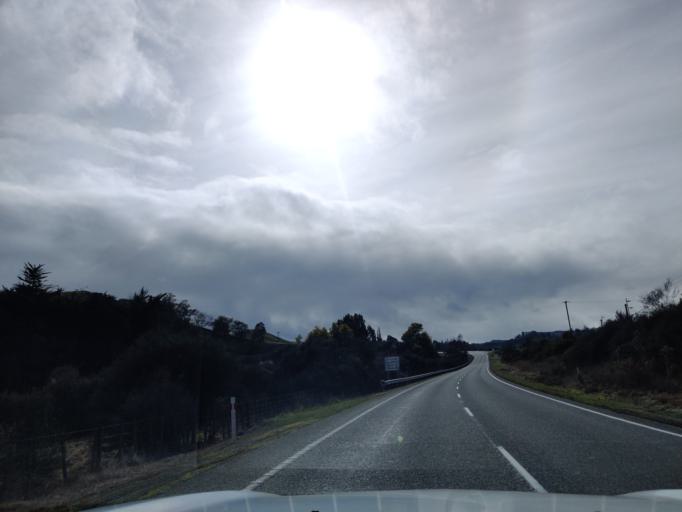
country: NZ
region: Manawatu-Wanganui
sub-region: Ruapehu District
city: Waiouru
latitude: -39.7550
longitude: 175.8302
